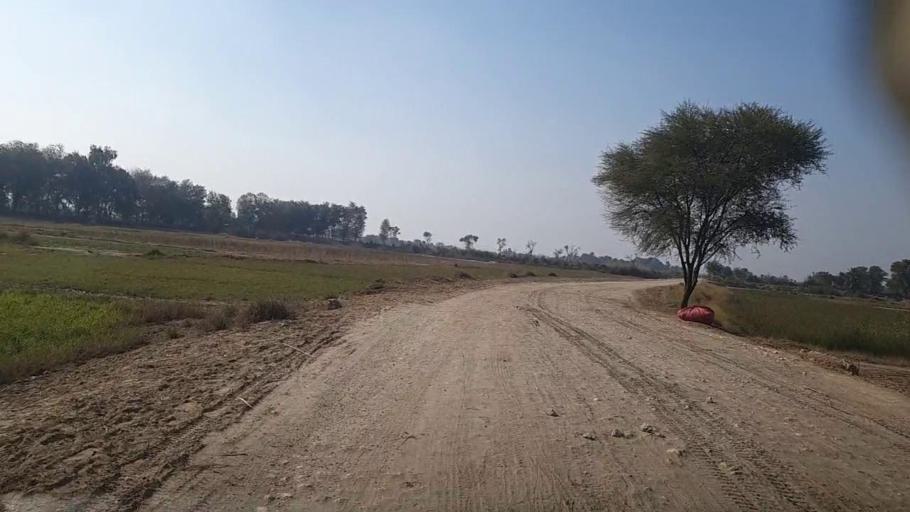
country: PK
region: Sindh
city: Mirpur Mathelo
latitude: 27.8989
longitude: 69.6465
